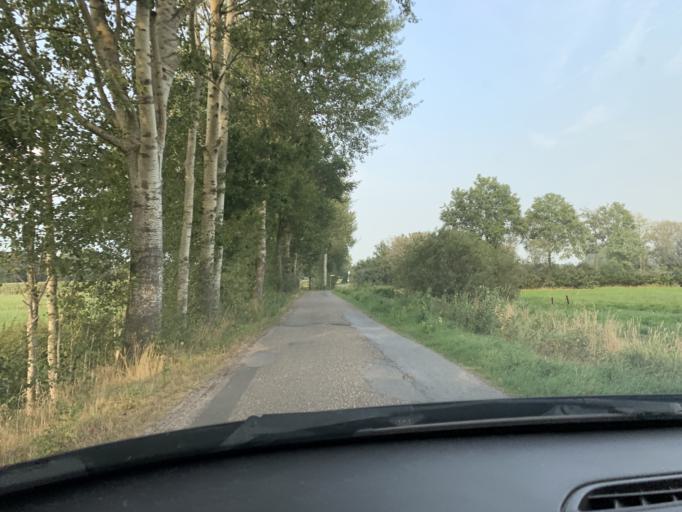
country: DE
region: Lower Saxony
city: Apen
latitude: 53.2418
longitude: 7.8257
